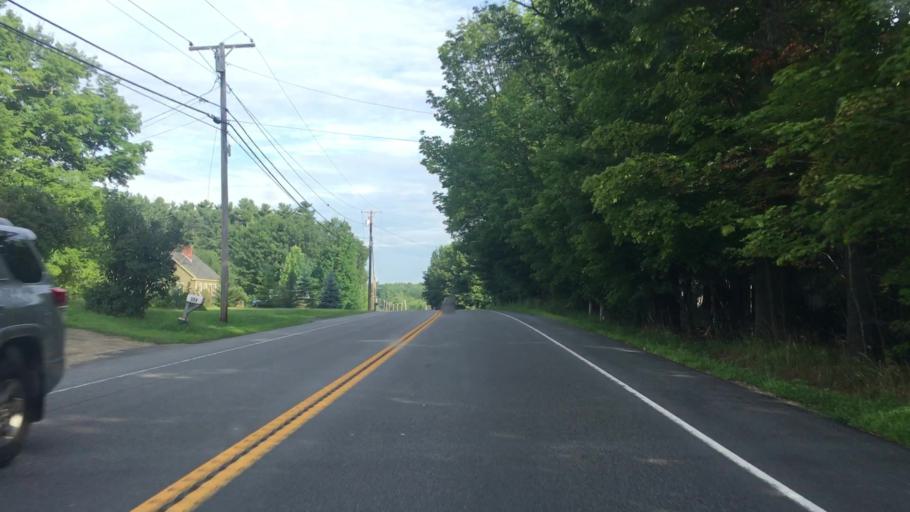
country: US
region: Maine
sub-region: Cumberland County
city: Gorham
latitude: 43.7048
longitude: -70.5045
